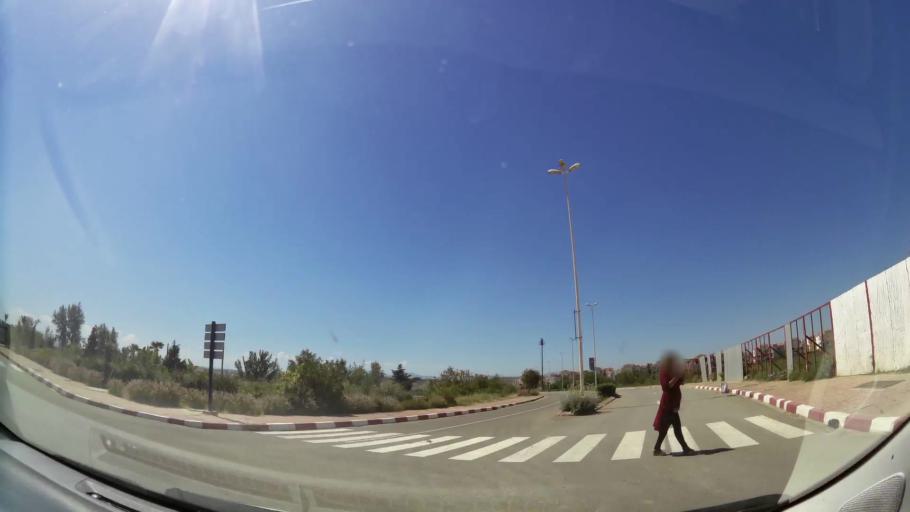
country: MA
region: Oriental
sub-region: Berkane-Taourirt
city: Madagh
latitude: 35.1082
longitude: -2.3114
